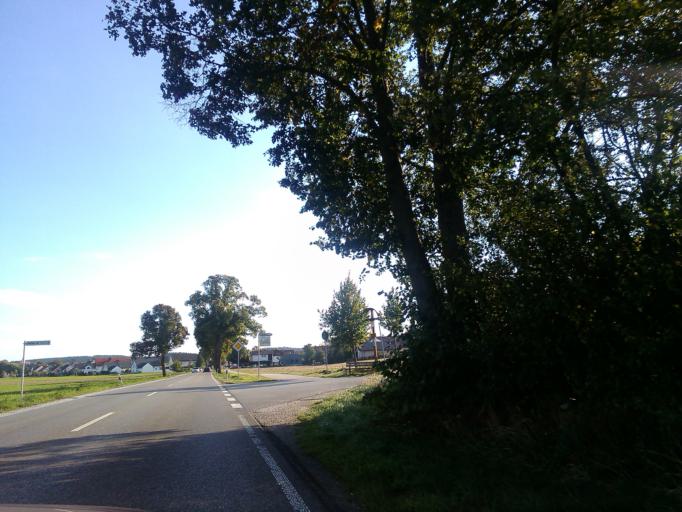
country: DE
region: Bavaria
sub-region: Upper Bavaria
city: Alling
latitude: 48.1492
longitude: 11.3018
